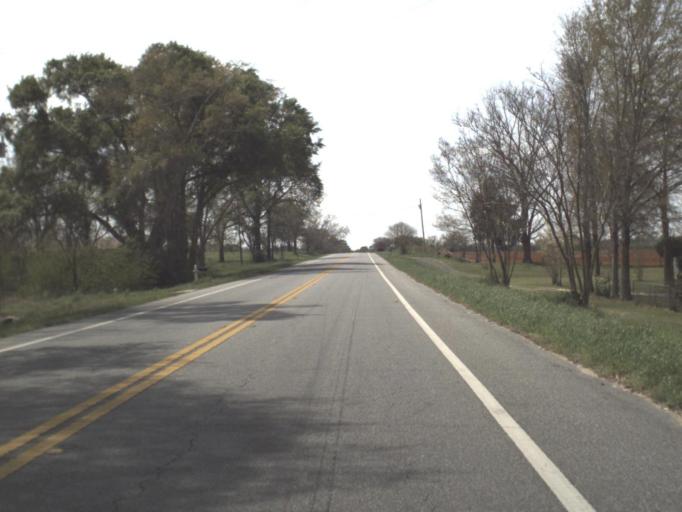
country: US
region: Florida
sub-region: Jackson County
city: Graceville
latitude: 30.9859
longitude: -85.4831
